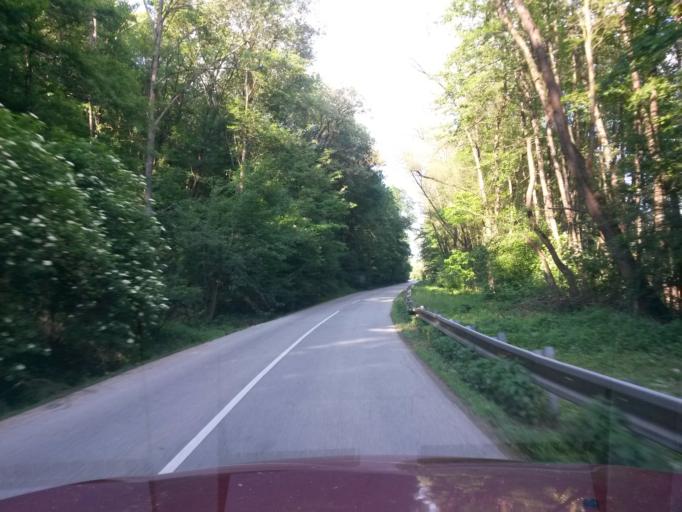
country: SK
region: Kosicky
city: Roznava
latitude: 48.5757
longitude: 20.6478
